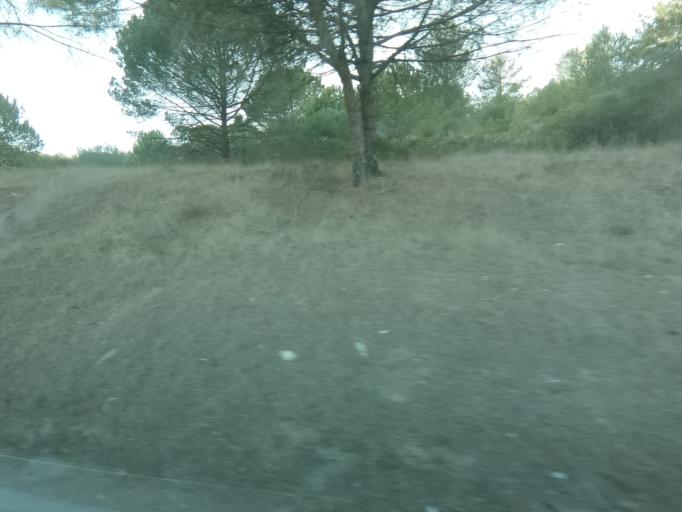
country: PT
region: Setubal
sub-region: Palmela
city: Quinta do Anjo
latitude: 38.5245
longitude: -8.9829
